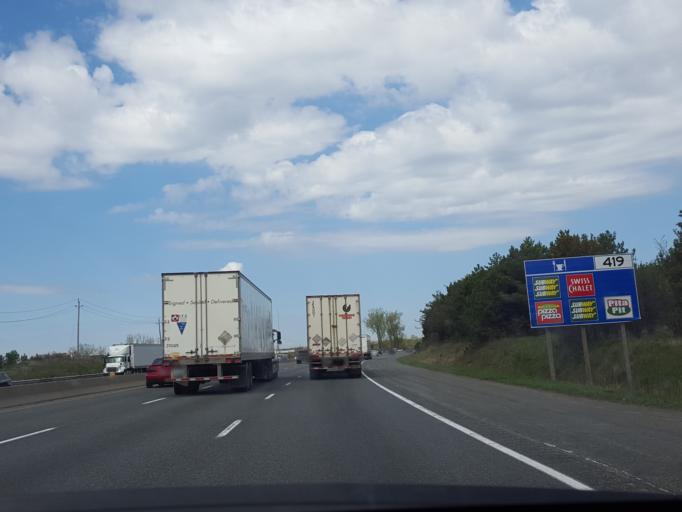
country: CA
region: Ontario
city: Oshawa
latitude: 43.8760
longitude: -78.7955
